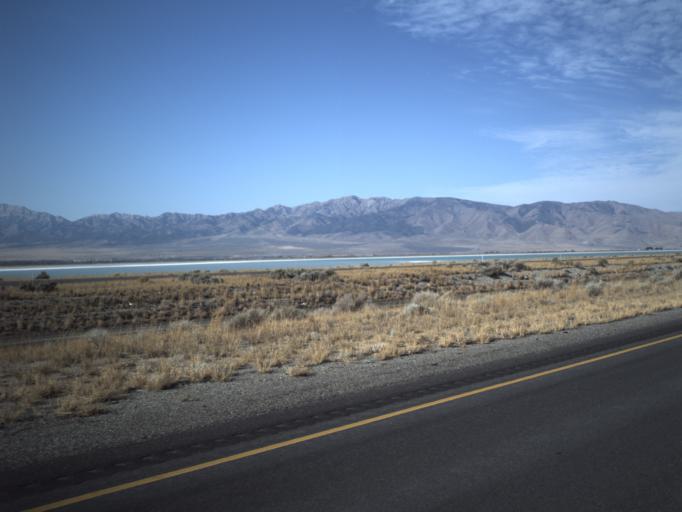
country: US
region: Utah
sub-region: Tooele County
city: Stansbury park
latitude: 40.6661
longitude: -112.3680
